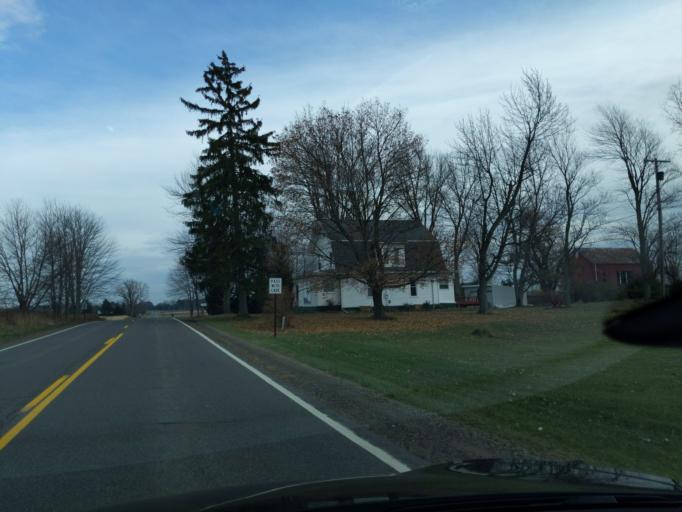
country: US
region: Michigan
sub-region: Ingham County
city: Mason
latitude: 42.6400
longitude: -84.3780
